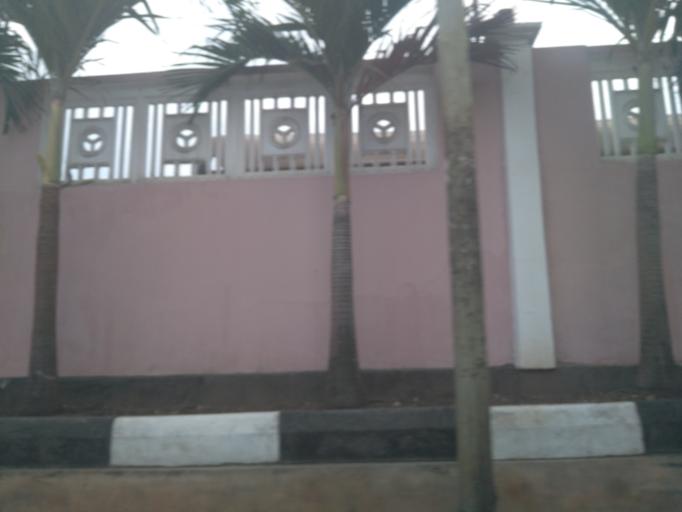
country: TZ
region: Dar es Salaam
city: Magomeni
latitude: -6.7932
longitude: 39.2659
